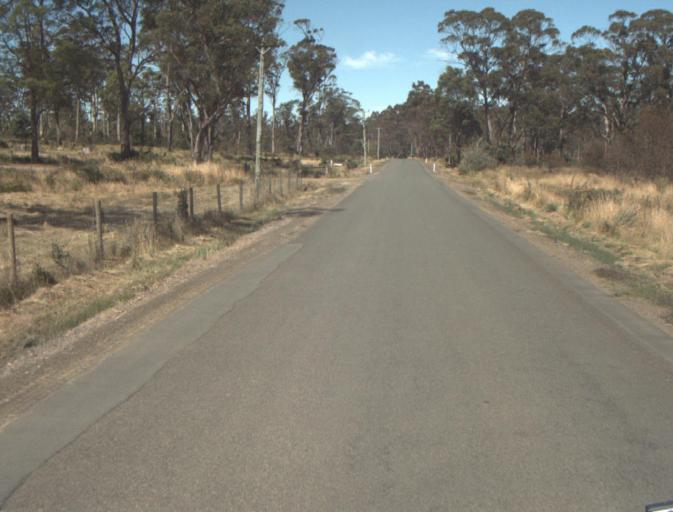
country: AU
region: Tasmania
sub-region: Launceston
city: Newstead
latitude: -41.3828
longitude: 147.2975
